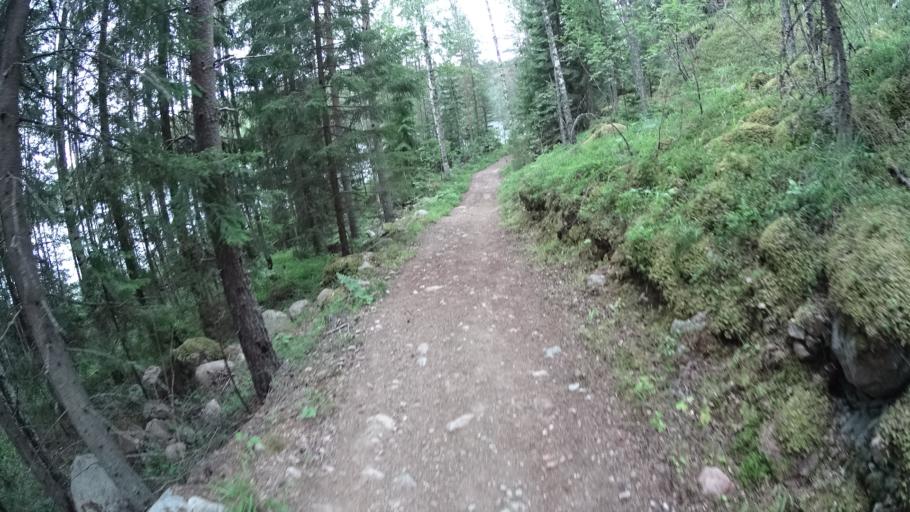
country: FI
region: Southern Savonia
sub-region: Mikkeli
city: Maentyharju
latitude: 61.1799
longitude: 26.8977
